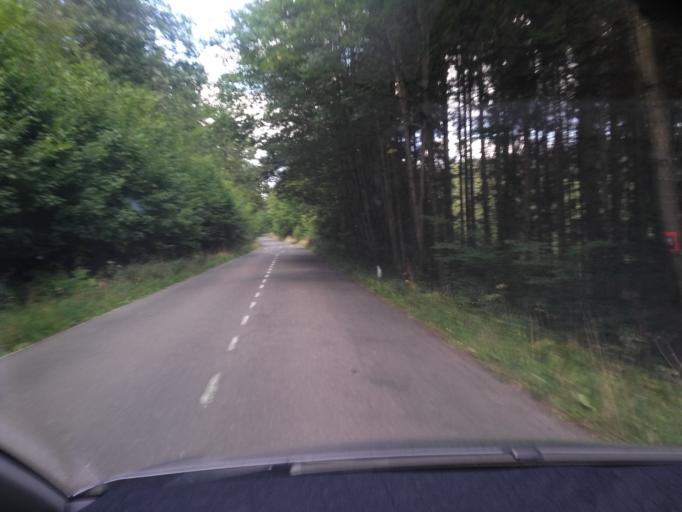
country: BE
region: Wallonia
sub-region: Province du Luxembourg
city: Libin
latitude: 50.0236
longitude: 5.3032
